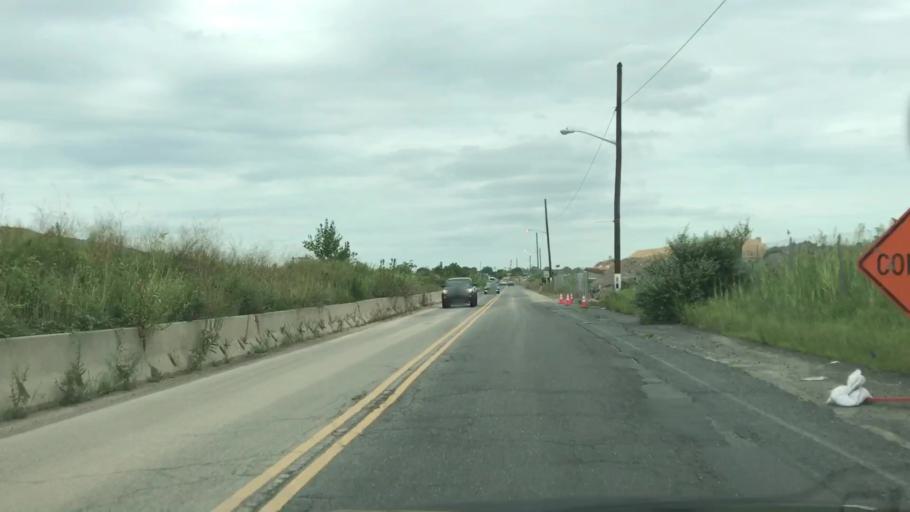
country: US
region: New Jersey
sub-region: Hudson County
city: Bayonne
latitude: 40.6685
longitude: -74.0925
